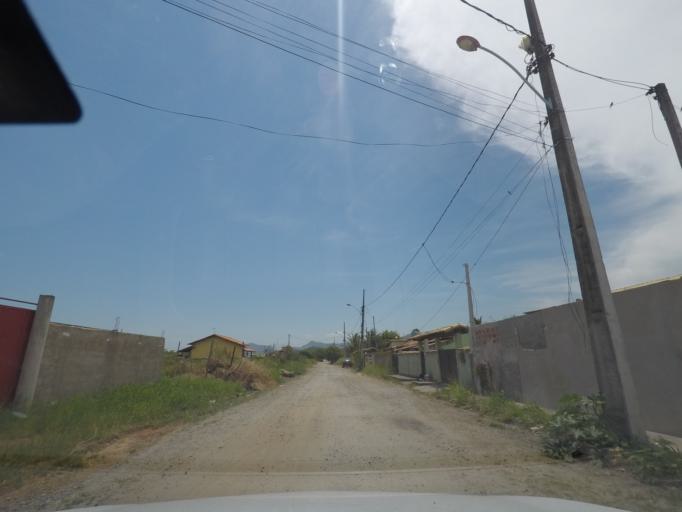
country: BR
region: Rio de Janeiro
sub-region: Marica
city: Marica
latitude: -22.9543
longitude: -42.9478
